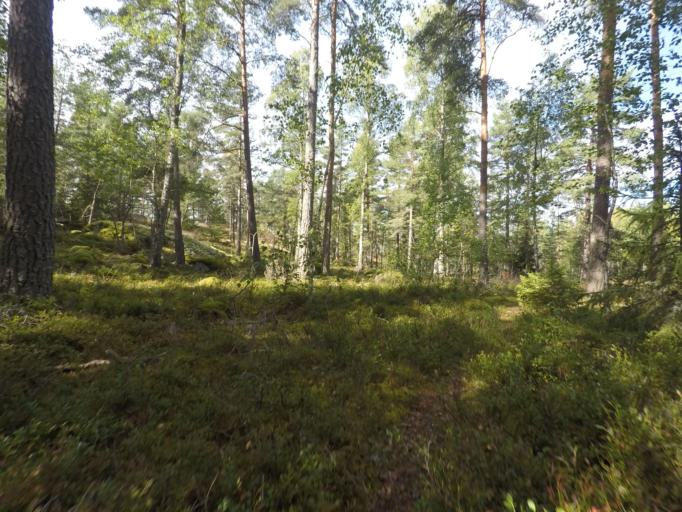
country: SE
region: Soedermanland
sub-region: Eskilstuna Kommun
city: Hallbybrunn
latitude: 59.4284
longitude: 16.4115
